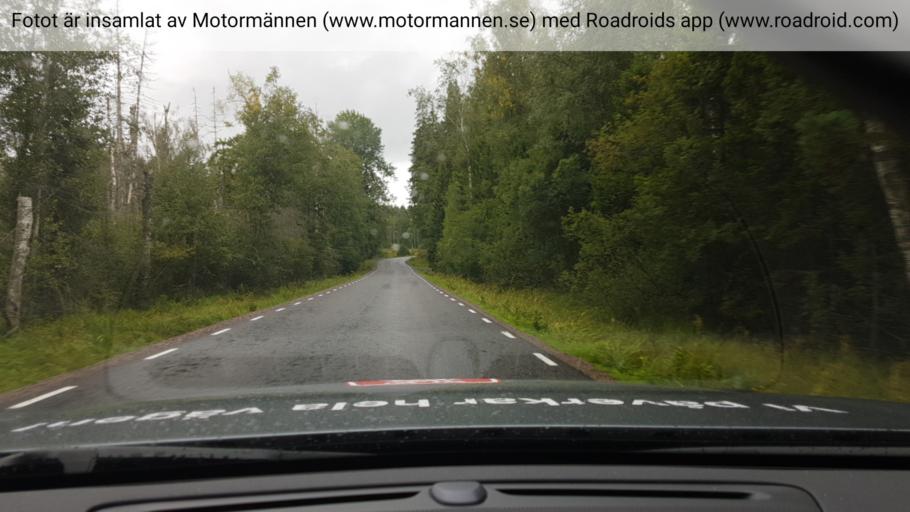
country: SE
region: Stockholm
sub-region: Nynashamns Kommun
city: Osmo
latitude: 59.0359
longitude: 17.9308
